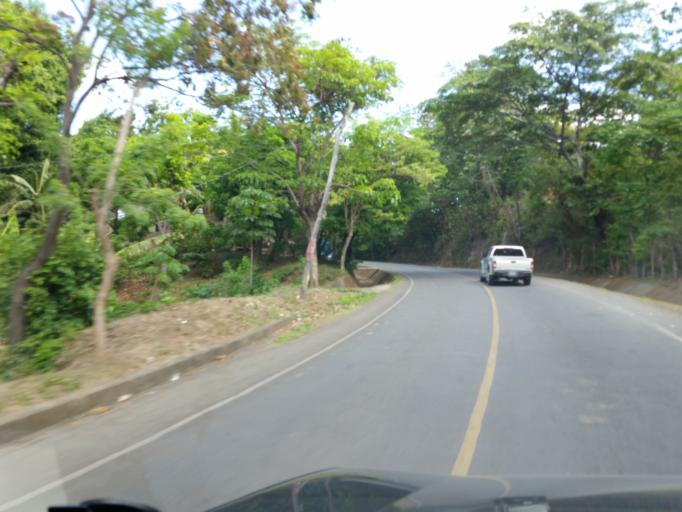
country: NI
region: Masaya
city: La Concepcion
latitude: 11.9568
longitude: -86.1917
